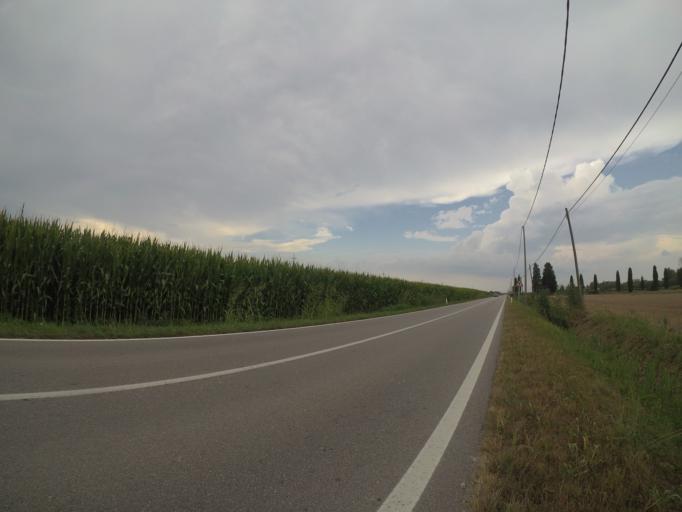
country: IT
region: Friuli Venezia Giulia
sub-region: Provincia di Udine
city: Pertegada
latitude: 45.7566
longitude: 13.0575
